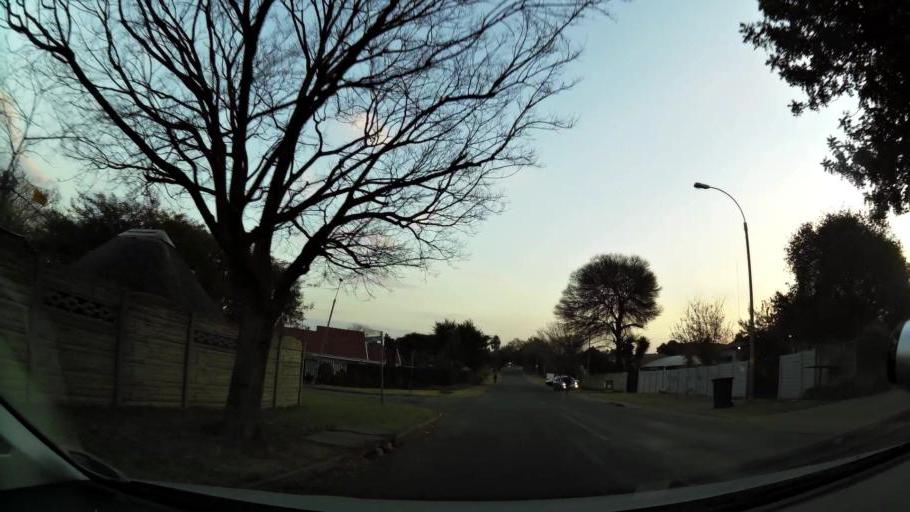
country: ZA
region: Gauteng
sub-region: Ekurhuleni Metropolitan Municipality
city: Tembisa
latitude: -26.0538
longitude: 28.2402
